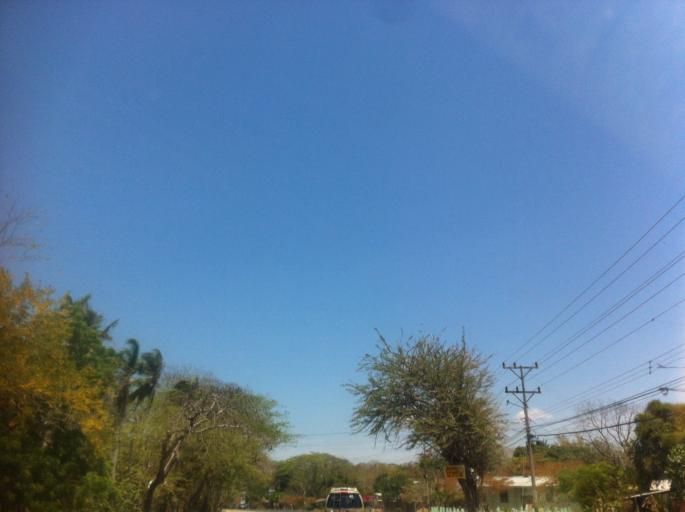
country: CR
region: Guanacaste
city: Sardinal
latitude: 10.5200
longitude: -85.5796
